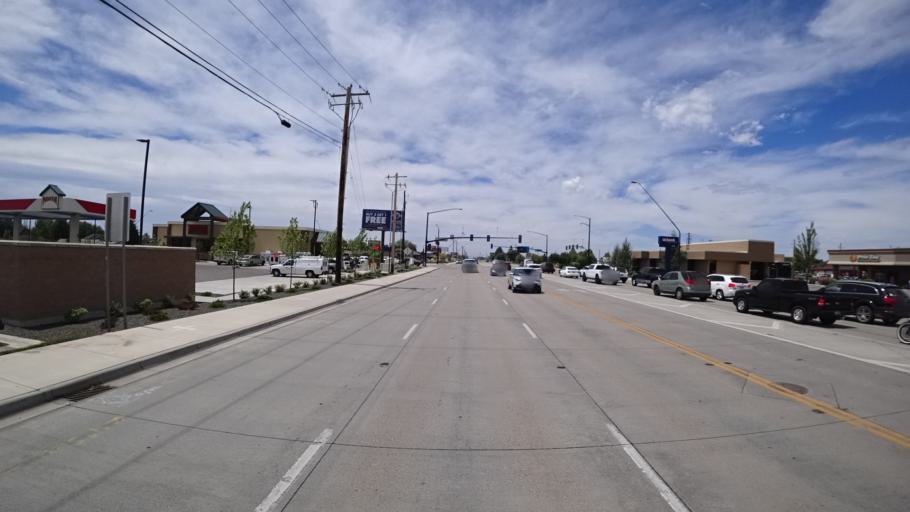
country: US
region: Idaho
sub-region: Ada County
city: Garden City
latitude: 43.6194
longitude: -116.3132
